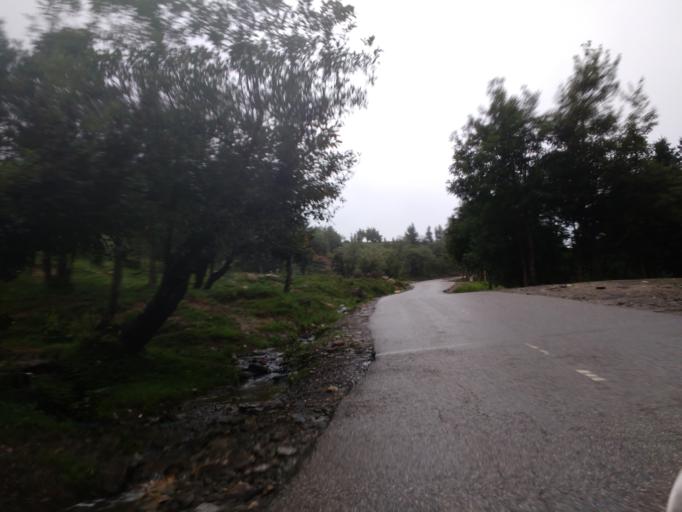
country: IN
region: Himachal Pradesh
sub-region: Kulu
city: Manali
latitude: 32.3316
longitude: 77.2046
